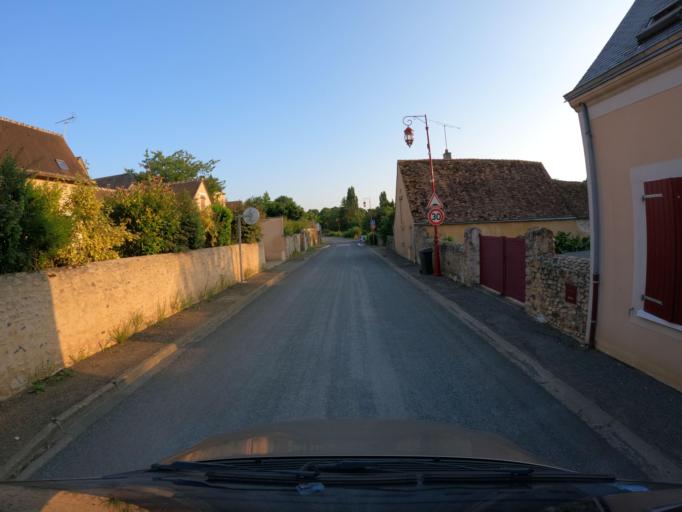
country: FR
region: Pays de la Loire
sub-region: Departement de la Sarthe
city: Parce-sur-Sarthe
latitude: 47.9035
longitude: -0.2217
